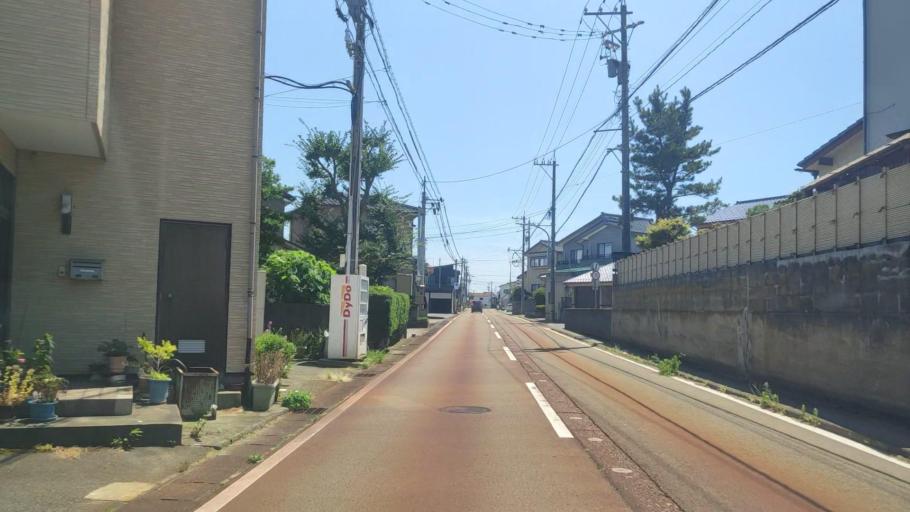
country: JP
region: Ishikawa
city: Kanazawa-shi
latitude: 36.6344
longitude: 136.6379
